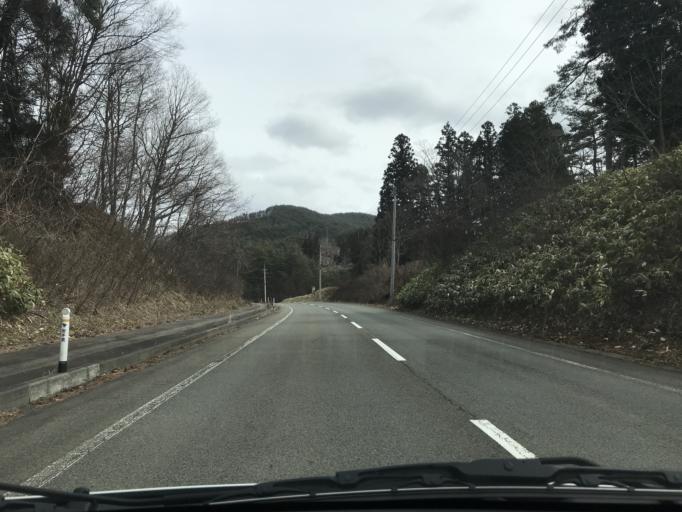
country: JP
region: Iwate
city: Tono
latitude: 39.2981
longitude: 141.3362
